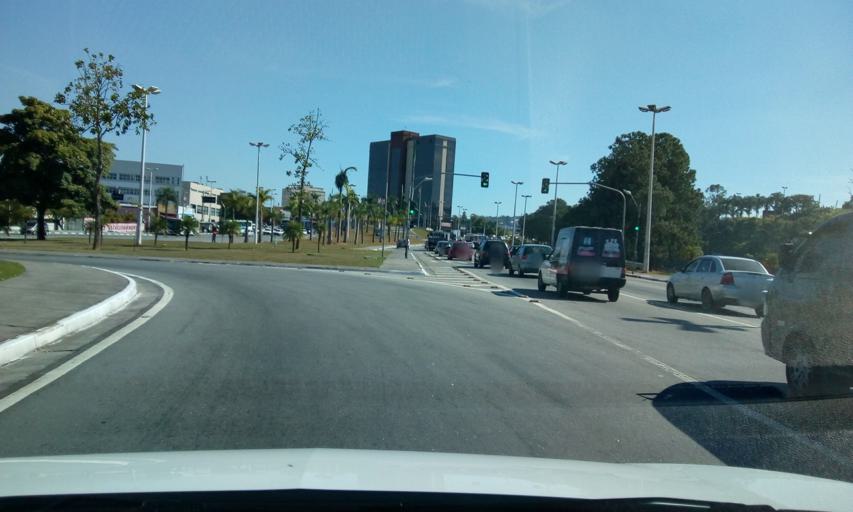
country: BR
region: Sao Paulo
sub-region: Barueri
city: Barueri
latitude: -23.5056
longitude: -46.8731
